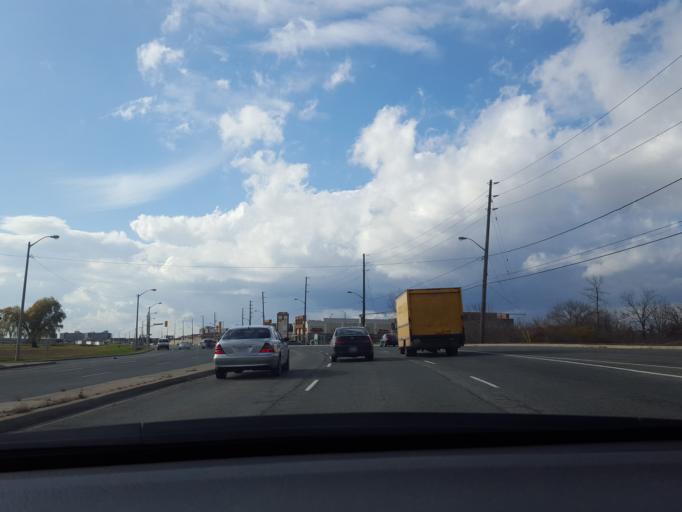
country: CA
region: Ontario
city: Etobicoke
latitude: 43.7207
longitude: -79.6103
